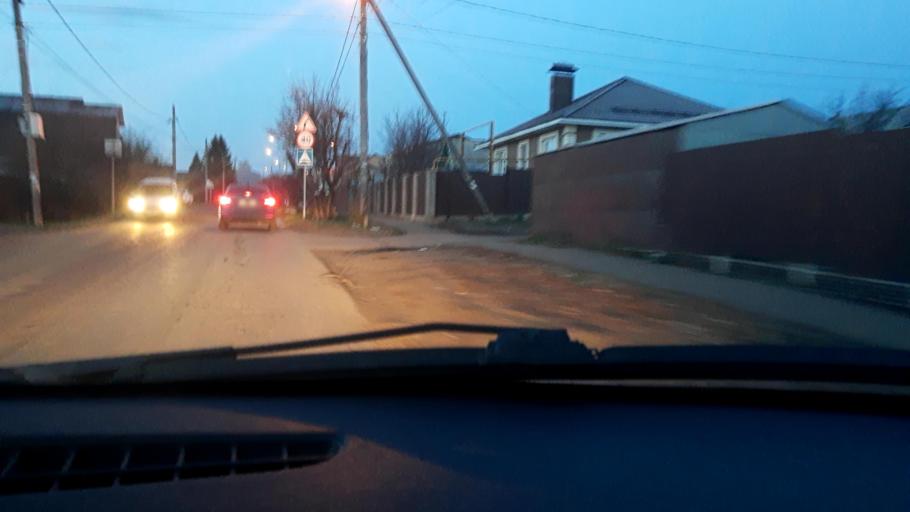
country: RU
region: Bashkortostan
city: Avdon
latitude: 54.6966
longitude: 55.8144
